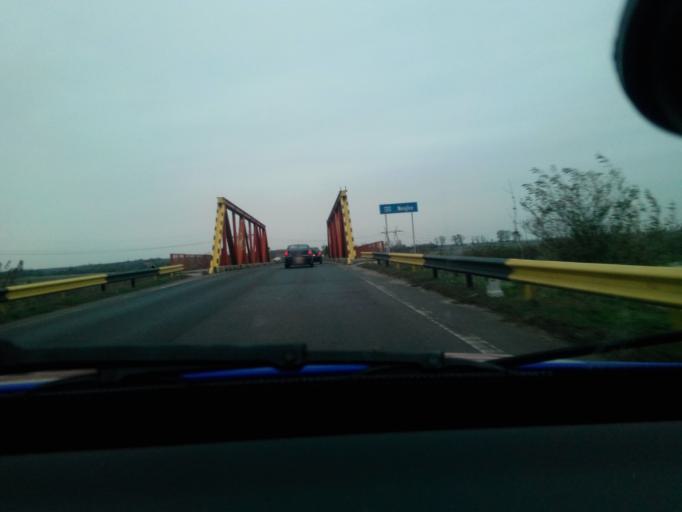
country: RO
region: Giurgiu
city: Iepuresti
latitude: 44.2756
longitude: 25.8581
